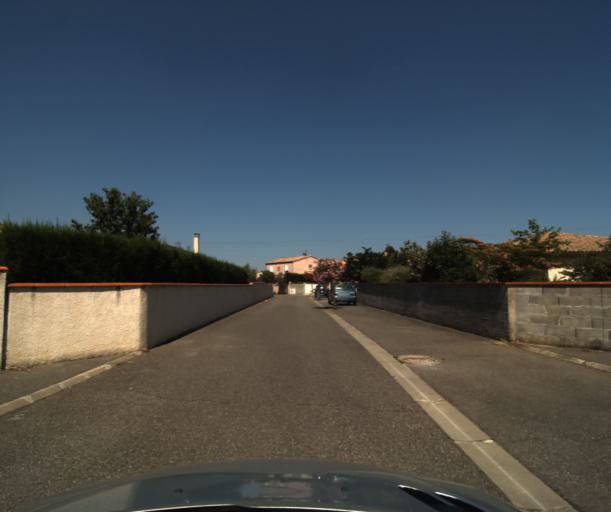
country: FR
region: Midi-Pyrenees
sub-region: Departement de la Haute-Garonne
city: Saubens
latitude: 43.4795
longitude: 1.3528
